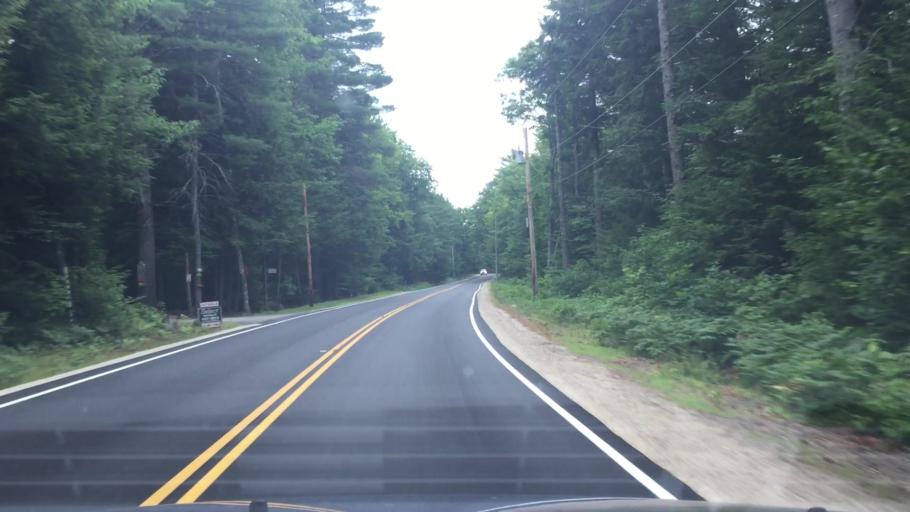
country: US
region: New Hampshire
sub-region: Carroll County
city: Freedom
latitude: 43.8396
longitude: -71.0802
